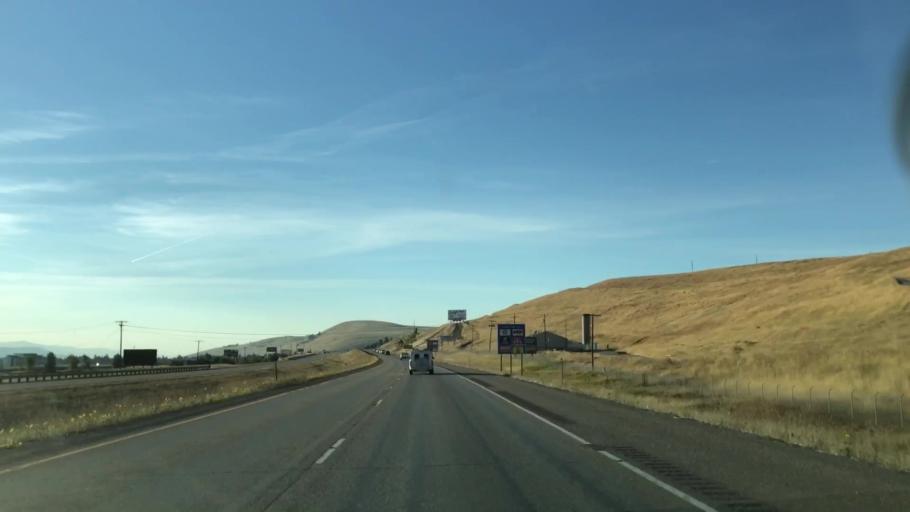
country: US
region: Montana
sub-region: Missoula County
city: Missoula
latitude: 46.9009
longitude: -114.0170
